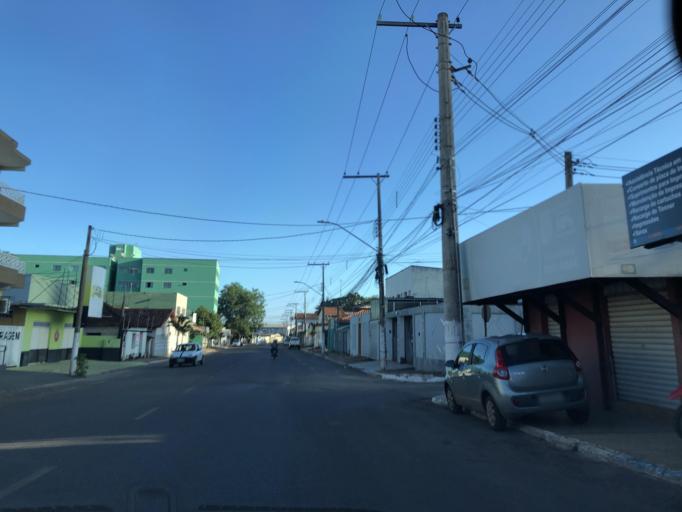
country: BR
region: Goias
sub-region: Luziania
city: Luziania
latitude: -16.2564
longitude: -47.9513
